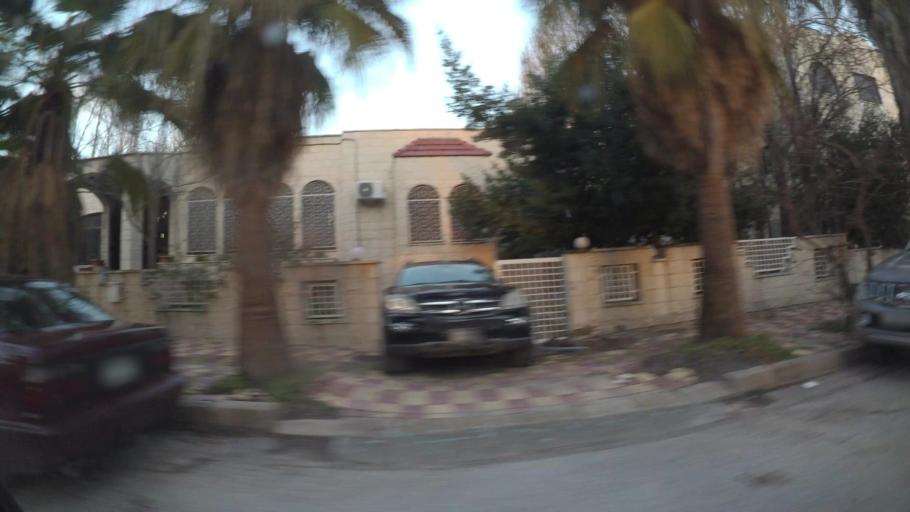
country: JO
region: Amman
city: Al Jubayhah
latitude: 32.0006
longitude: 35.8525
